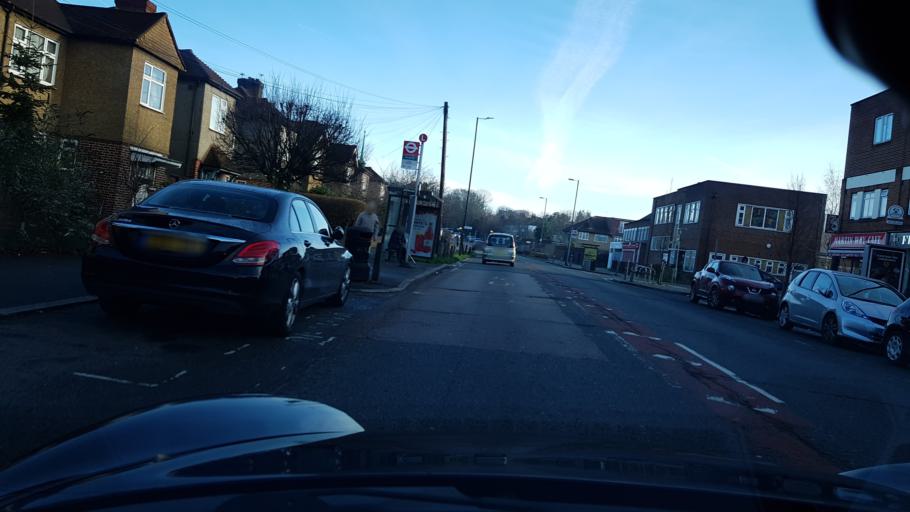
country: GB
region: England
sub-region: Greater London
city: Morden
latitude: 51.4029
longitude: -0.2102
